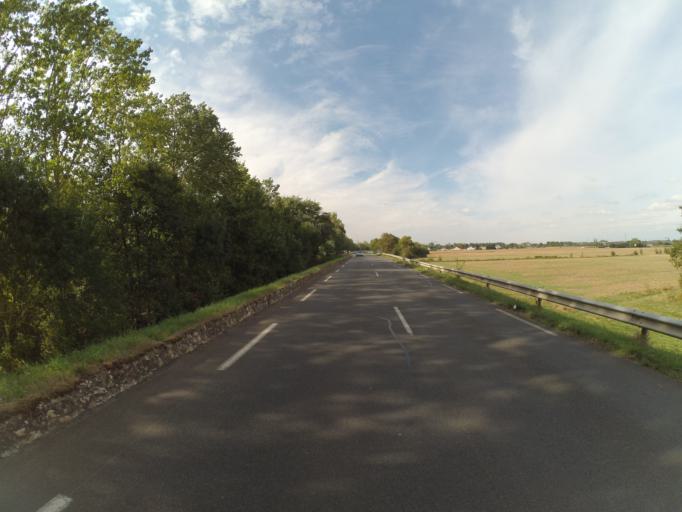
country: FR
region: Pays de la Loire
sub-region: Departement de Maine-et-Loire
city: Varennes-sur-Loire
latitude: 47.2264
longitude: 0.0639
